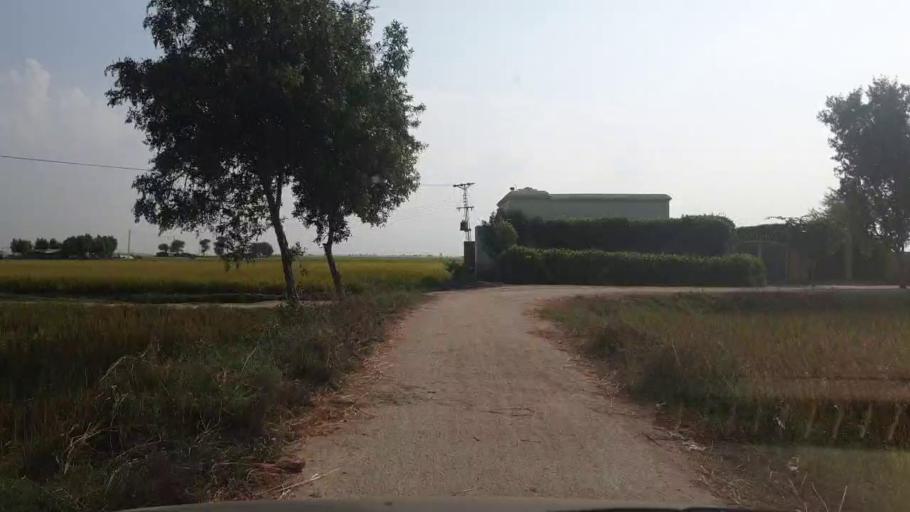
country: PK
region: Sindh
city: Kario
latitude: 24.6349
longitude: 68.5580
